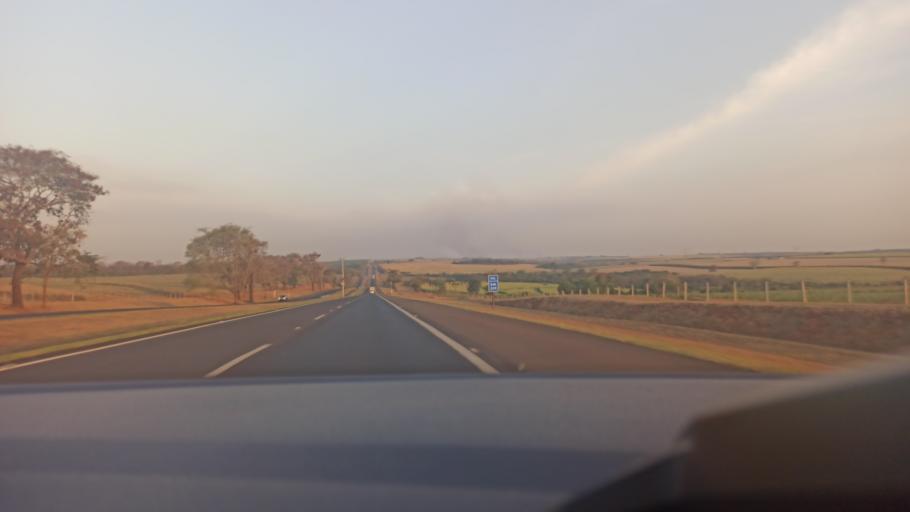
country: BR
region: Sao Paulo
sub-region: Taquaritinga
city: Taquaritinga
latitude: -21.4237
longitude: -48.6739
